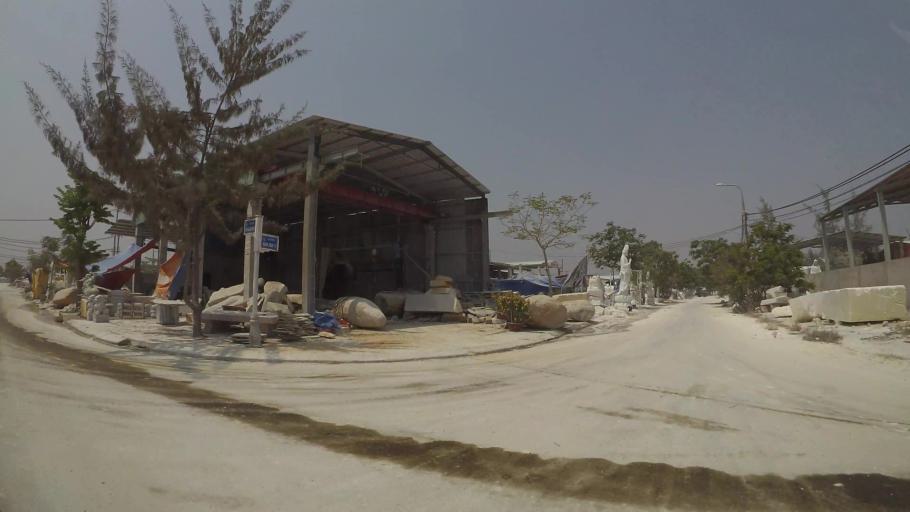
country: VN
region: Da Nang
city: Ngu Hanh Son
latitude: 15.9901
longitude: 108.2518
